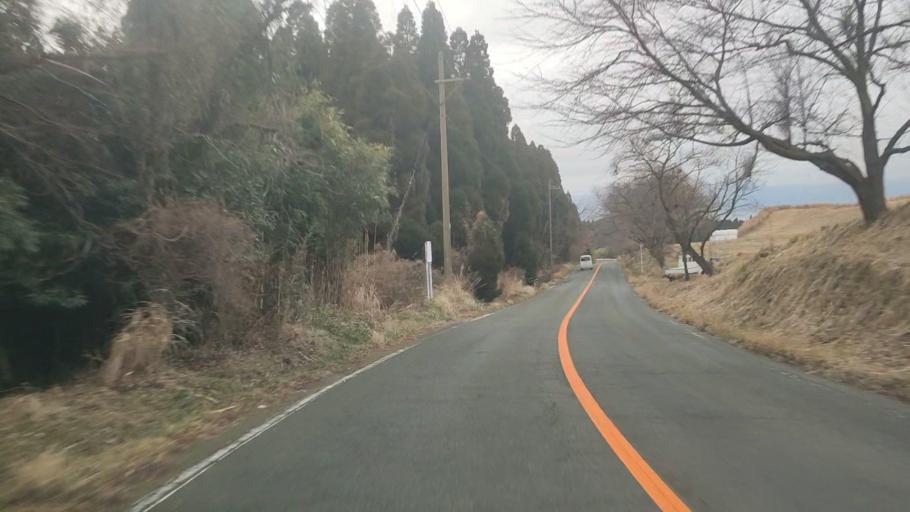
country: JP
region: Kumamoto
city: Aso
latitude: 32.9098
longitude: 131.1346
